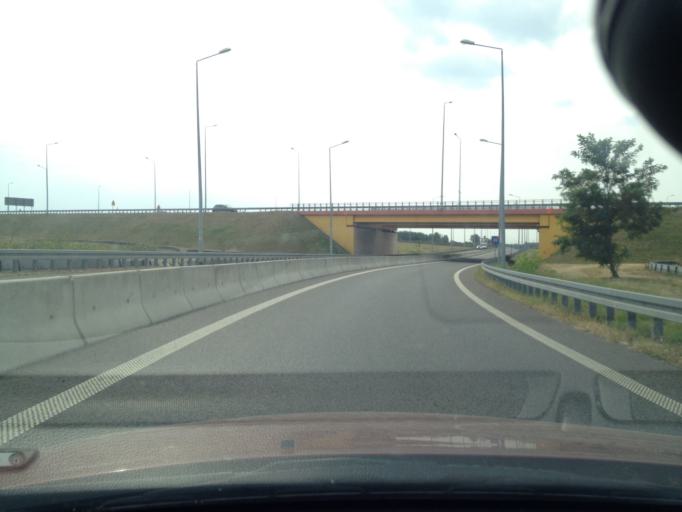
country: PL
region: West Pomeranian Voivodeship
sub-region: Powiat pyrzycki
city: Lipiany
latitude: 52.9526
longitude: 14.9510
